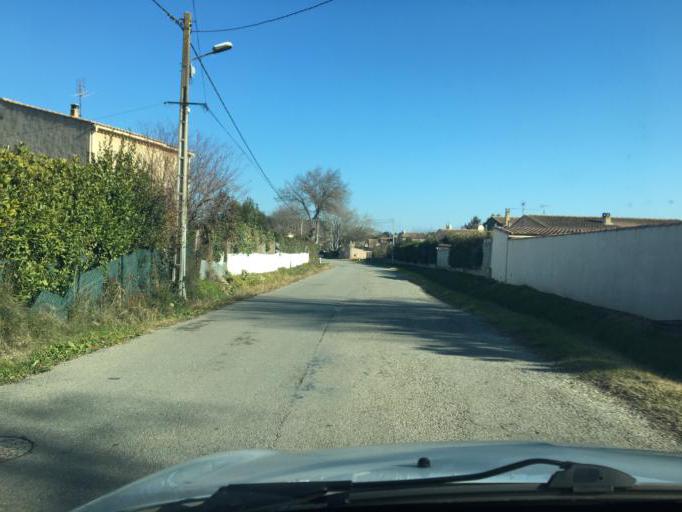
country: FR
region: Languedoc-Roussillon
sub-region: Departement du Gard
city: Les Angles
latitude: 43.9464
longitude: 4.7793
